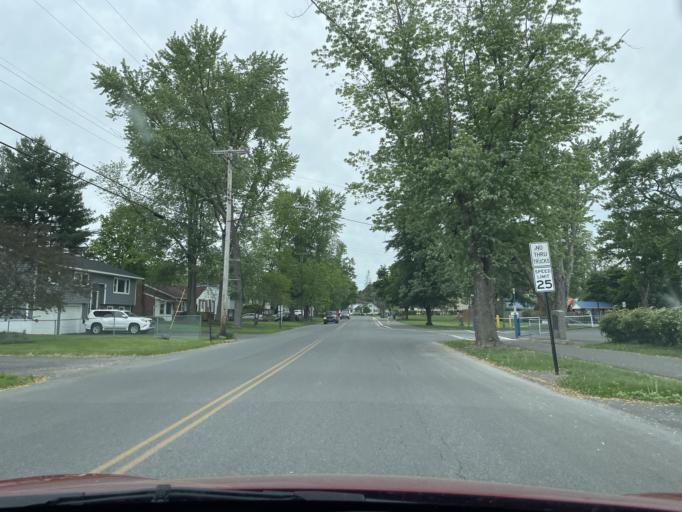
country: US
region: New York
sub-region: Ulster County
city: Saugerties
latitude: 42.0852
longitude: -73.9518
